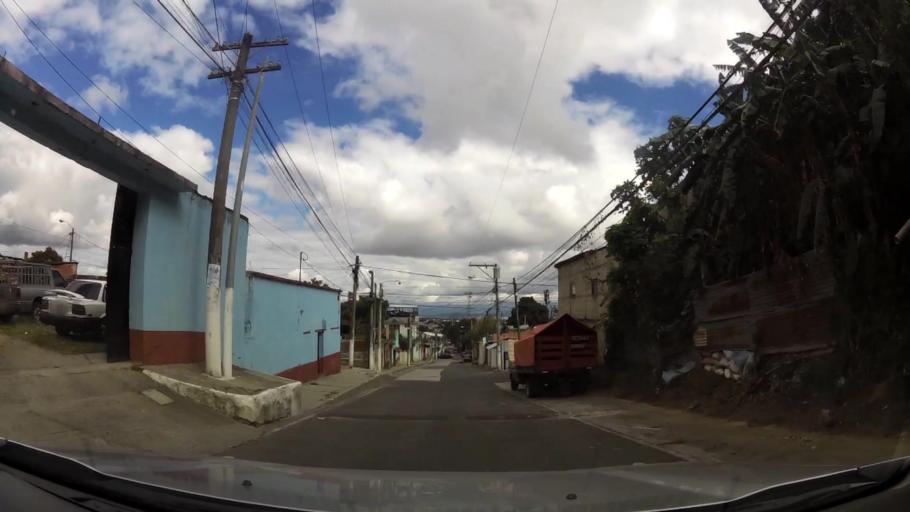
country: GT
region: Guatemala
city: Mixco
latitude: 14.6305
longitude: -90.6030
